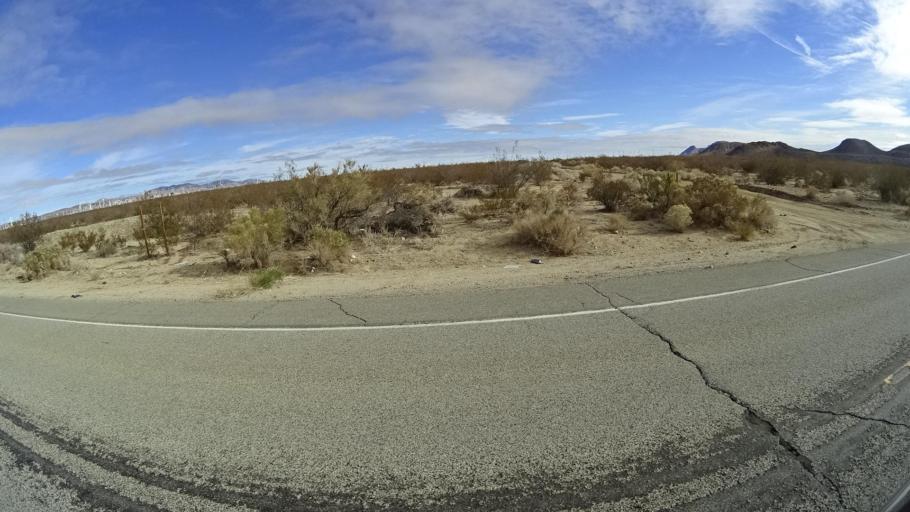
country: US
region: California
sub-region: Kern County
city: Mojave
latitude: 34.9753
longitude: -118.3088
